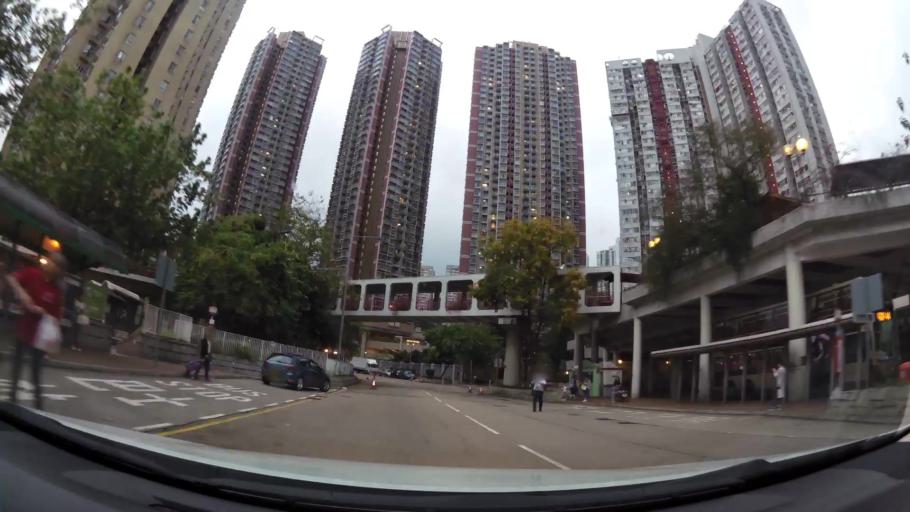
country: HK
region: Tsuen Wan
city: Tsuen Wan
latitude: 22.3542
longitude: 114.1040
